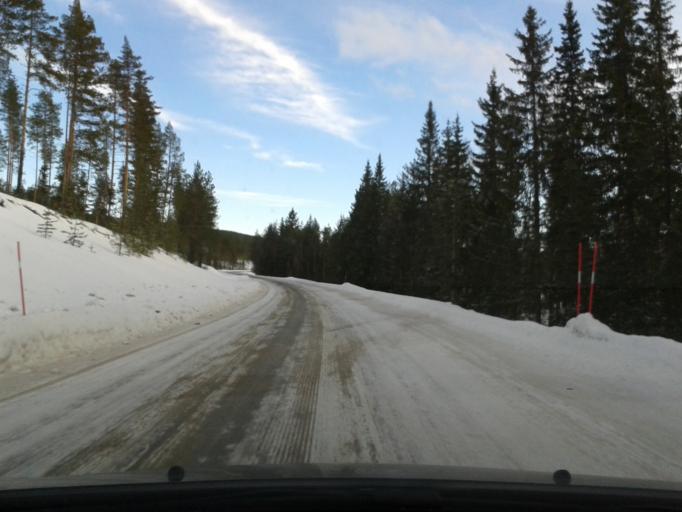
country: SE
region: Vaesterbotten
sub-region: Asele Kommun
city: Asele
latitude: 64.2474
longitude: 17.2815
